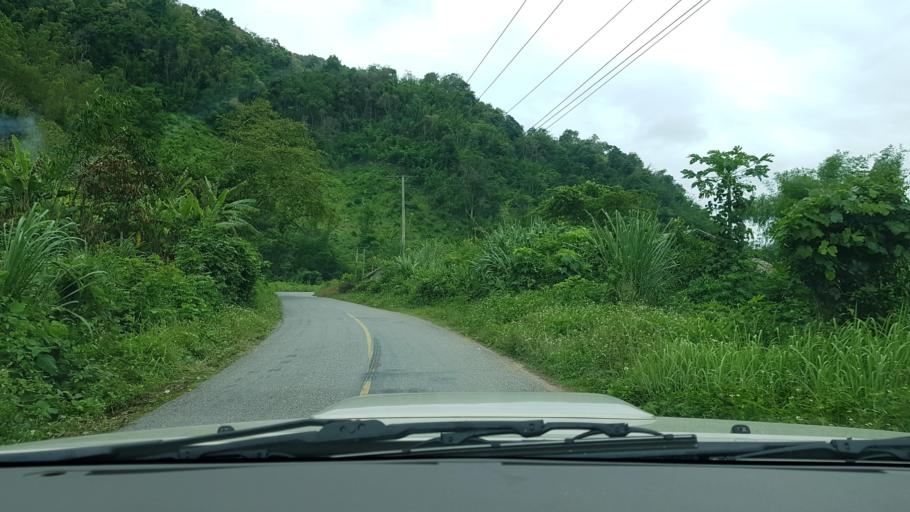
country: LA
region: Oudomxai
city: Muang La
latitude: 20.8237
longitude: 102.0961
